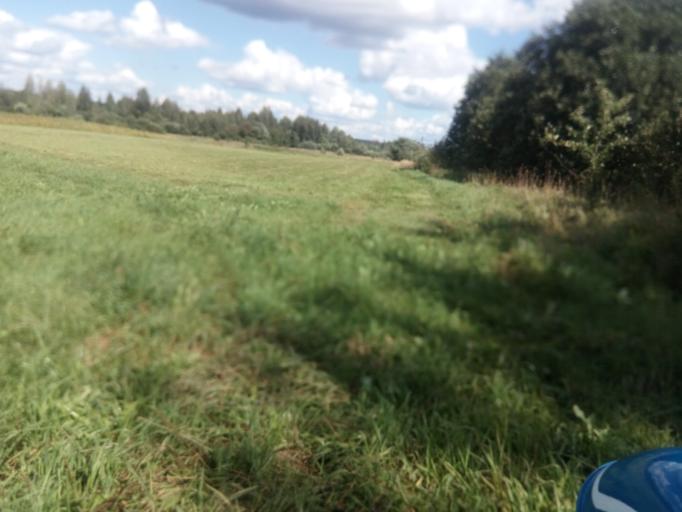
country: BY
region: Vitebsk
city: Dzisna
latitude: 55.6780
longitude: 28.3243
